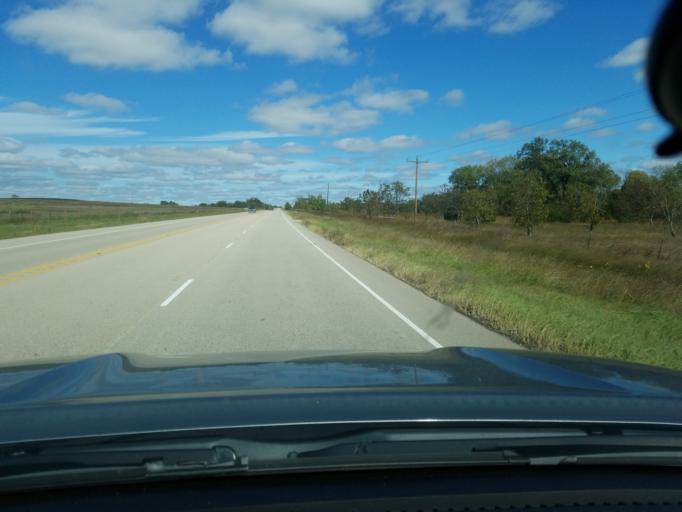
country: US
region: Texas
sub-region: Hamilton County
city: Hamilton
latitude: 31.6468
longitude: -98.1472
